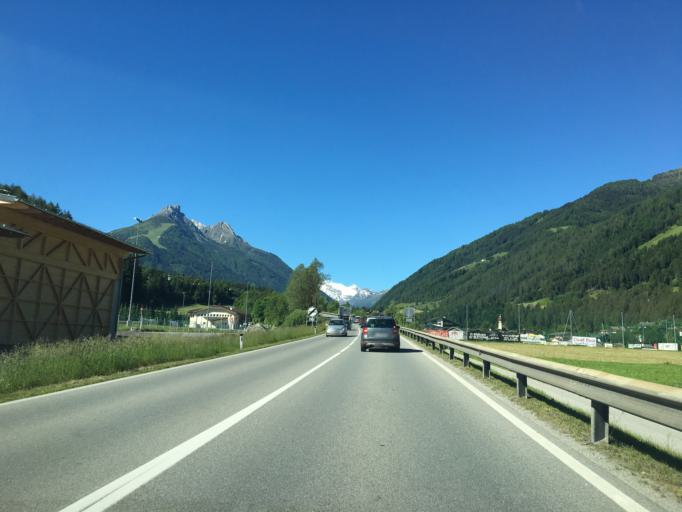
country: AT
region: Tyrol
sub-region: Politischer Bezirk Innsbruck Land
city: Fulpmes
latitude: 47.1458
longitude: 11.3489
